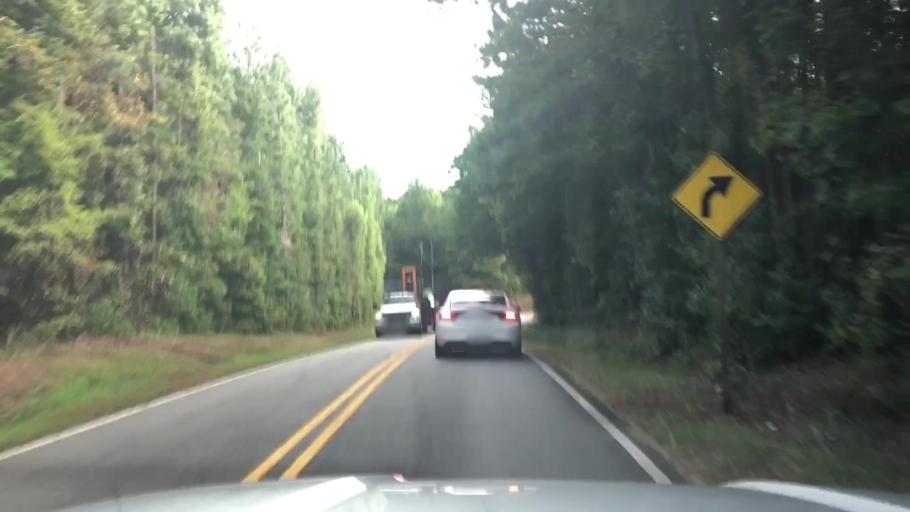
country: US
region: Georgia
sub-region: Bartow County
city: Euharlee
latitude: 34.0466
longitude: -84.8659
